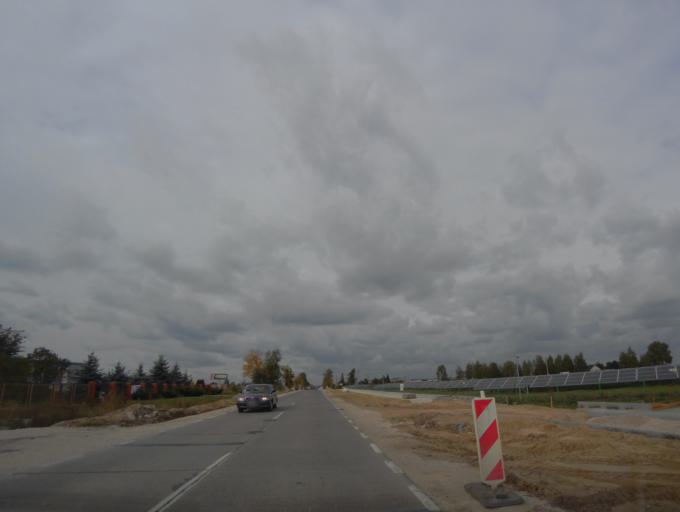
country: PL
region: Lublin Voivodeship
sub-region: Powiat wlodawski
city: Wlodawa
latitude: 51.5539
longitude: 23.5316
